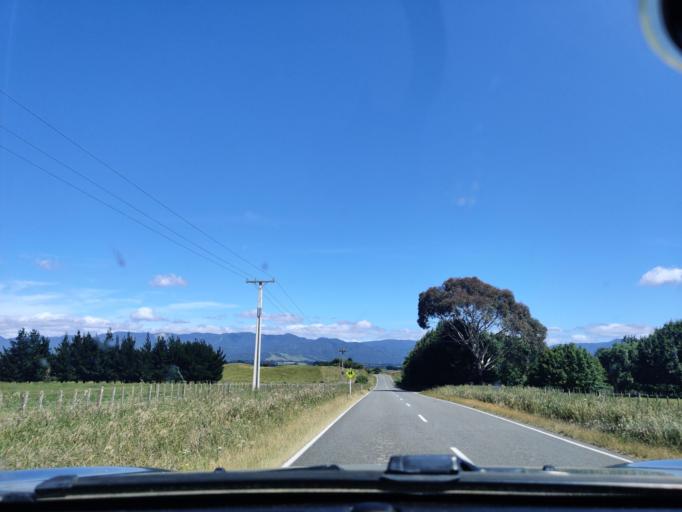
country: NZ
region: Wellington
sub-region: Upper Hutt City
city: Upper Hutt
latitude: -41.3284
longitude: 175.2313
